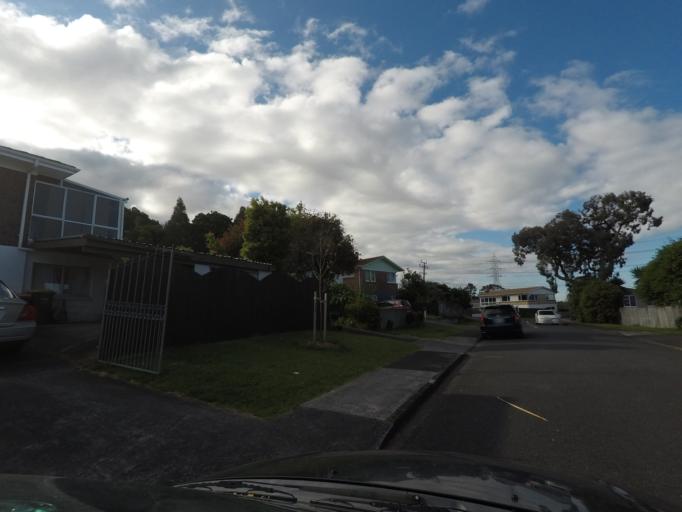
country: NZ
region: Auckland
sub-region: Auckland
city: Rosebank
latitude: -36.8802
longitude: 174.6549
